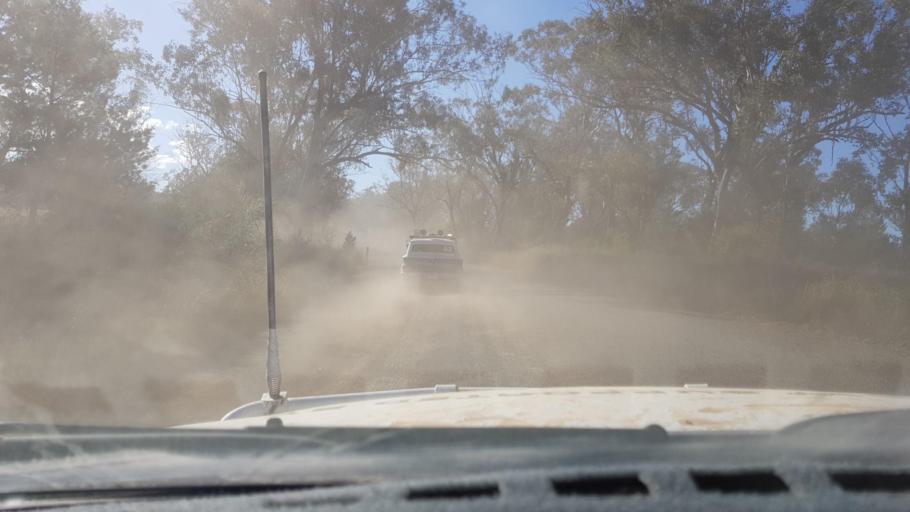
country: AU
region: New South Wales
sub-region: Tamworth Municipality
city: Manilla
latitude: -30.6592
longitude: 150.4805
